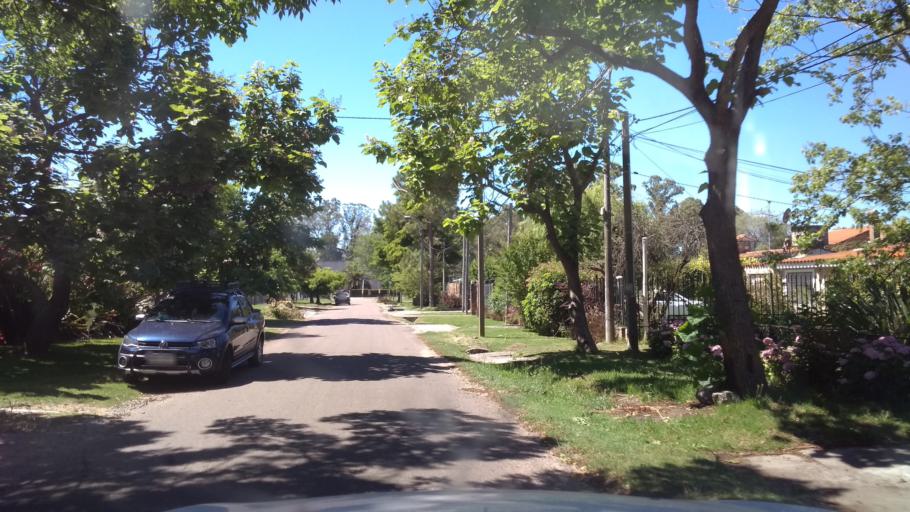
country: UY
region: Canelones
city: Paso de Carrasco
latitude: -34.8690
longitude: -56.0616
